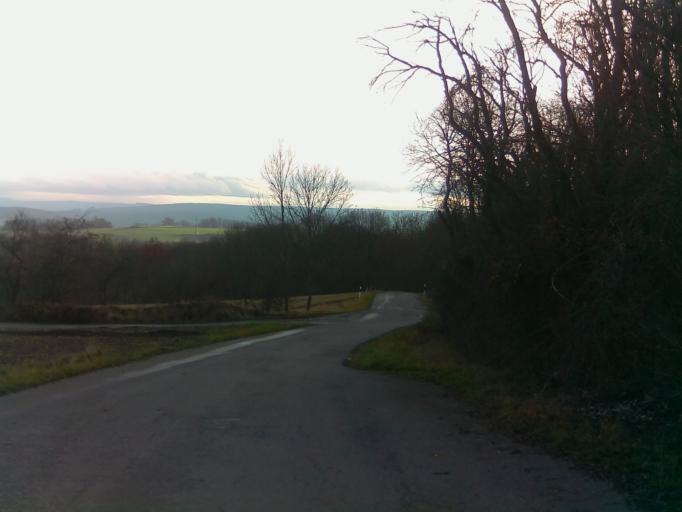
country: DE
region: Thuringia
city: Gumperda
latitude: 50.7996
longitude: 11.5147
